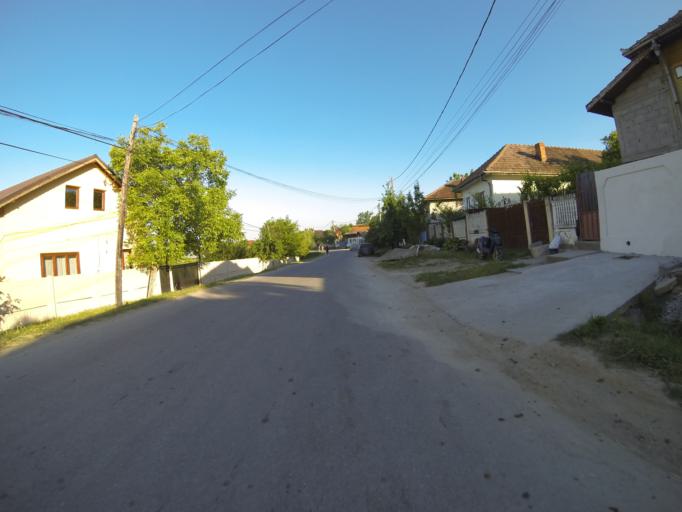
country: RO
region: Dolj
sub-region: Comuna Tuglui
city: Tuglui
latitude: 44.1984
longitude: 23.8019
